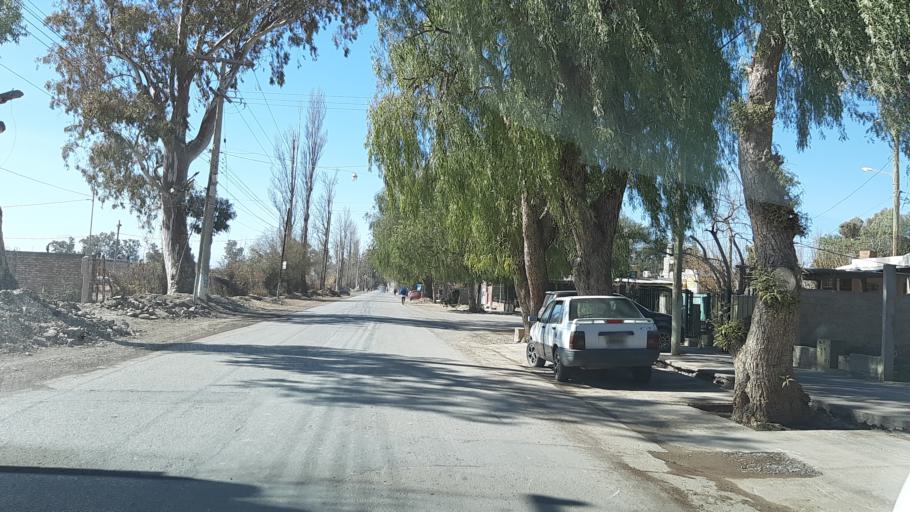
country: AR
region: San Juan
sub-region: Departamento de Zonda
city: Zonda
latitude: -31.4695
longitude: -68.7454
